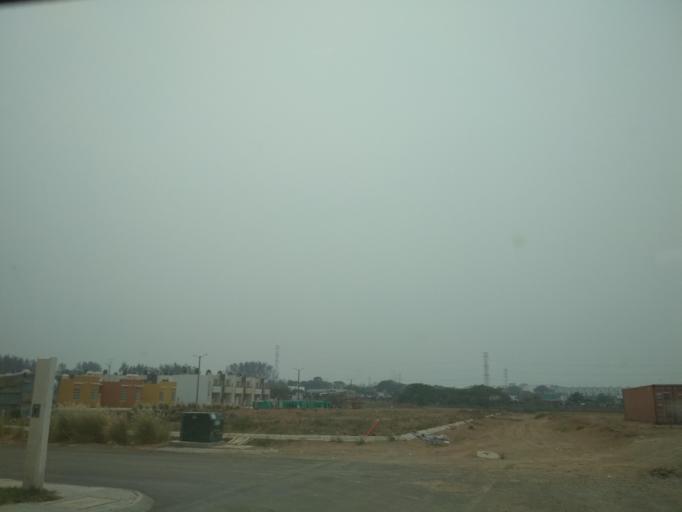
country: MX
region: Veracruz
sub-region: Veracruz
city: Las Amapolas
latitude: 19.1535
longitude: -96.2168
